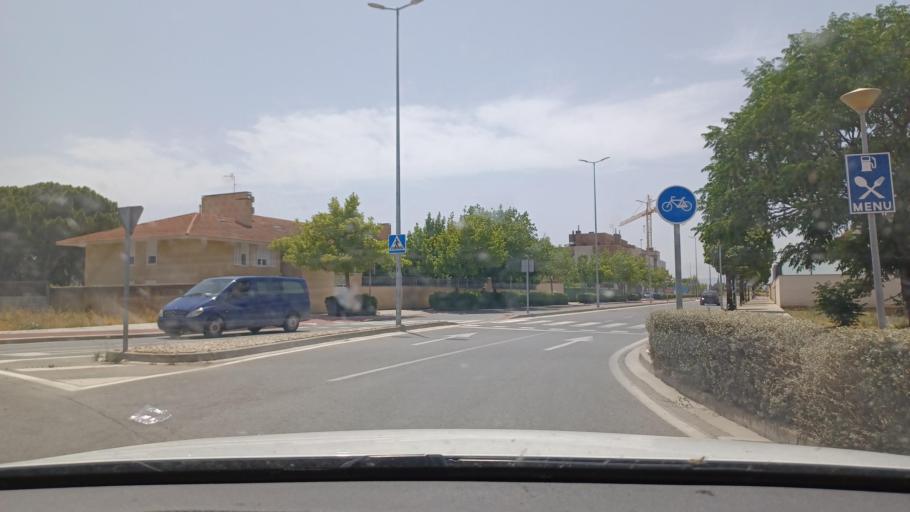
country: ES
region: Navarre
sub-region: Provincia de Navarra
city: Tudela
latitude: 42.0631
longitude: -1.6178
